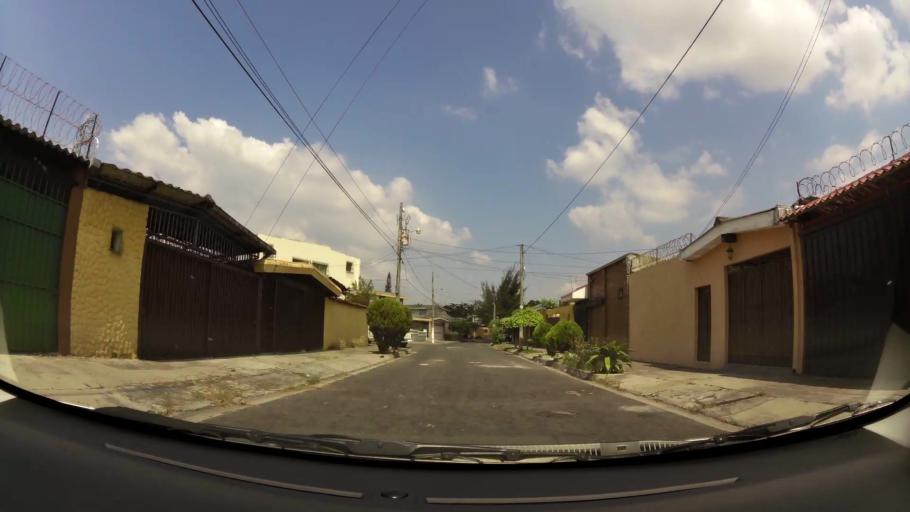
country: SV
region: San Salvador
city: Mejicanos
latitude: 13.7096
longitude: -89.2171
